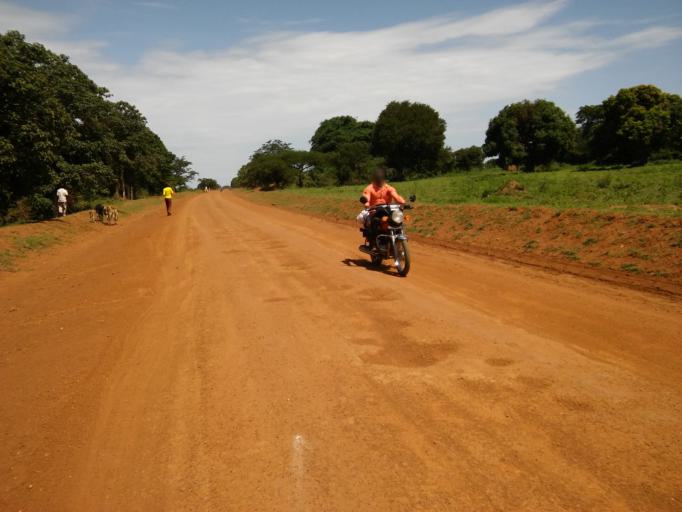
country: UG
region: Eastern Region
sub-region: Kumi District
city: Kumi
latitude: 1.4830
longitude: 33.9072
